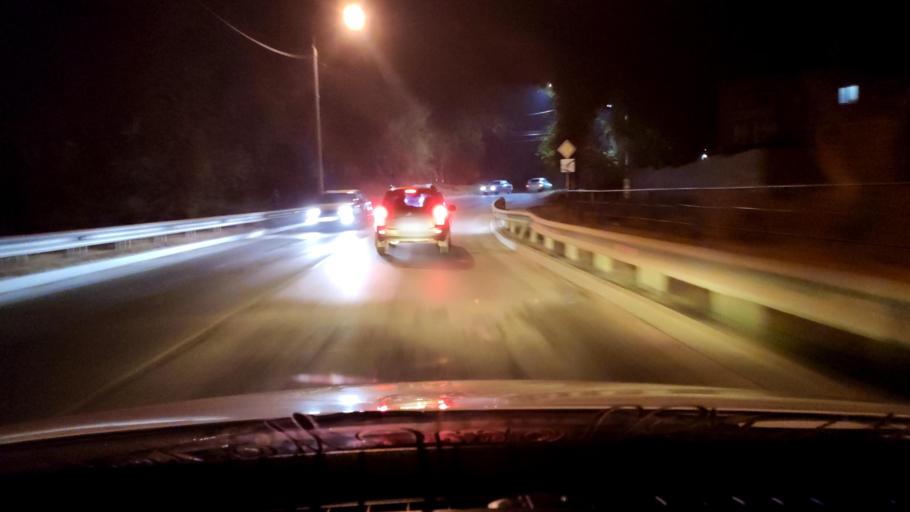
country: RU
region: Voronezj
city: Semiluki
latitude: 51.6768
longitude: 39.0306
